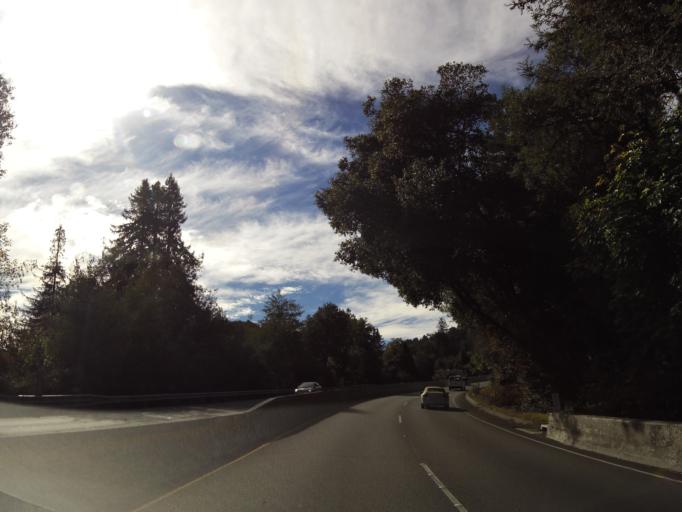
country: US
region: California
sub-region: Santa Clara County
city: Lexington Hills
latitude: 37.1574
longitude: -121.9822
